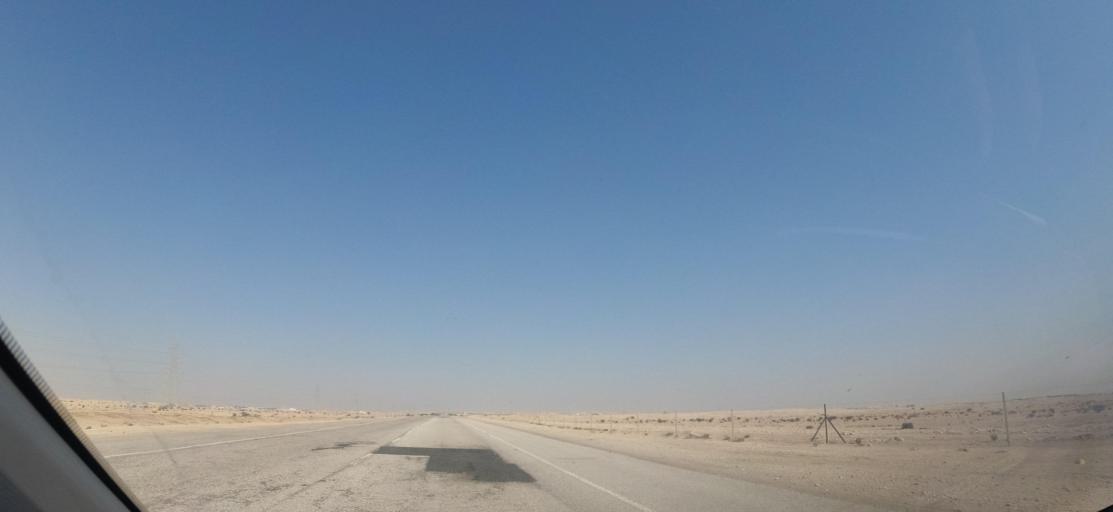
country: QA
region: Baladiyat ar Rayyan
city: Dukhan
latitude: 25.4763
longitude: 50.9466
